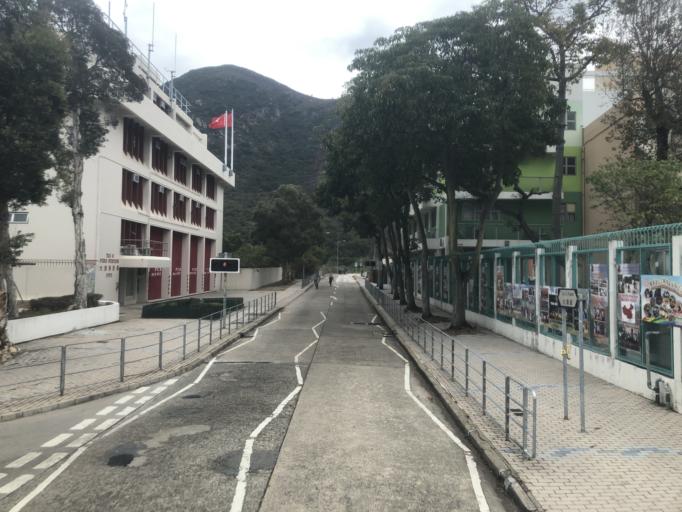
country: HK
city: Tai O
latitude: 22.2522
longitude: 113.8661
